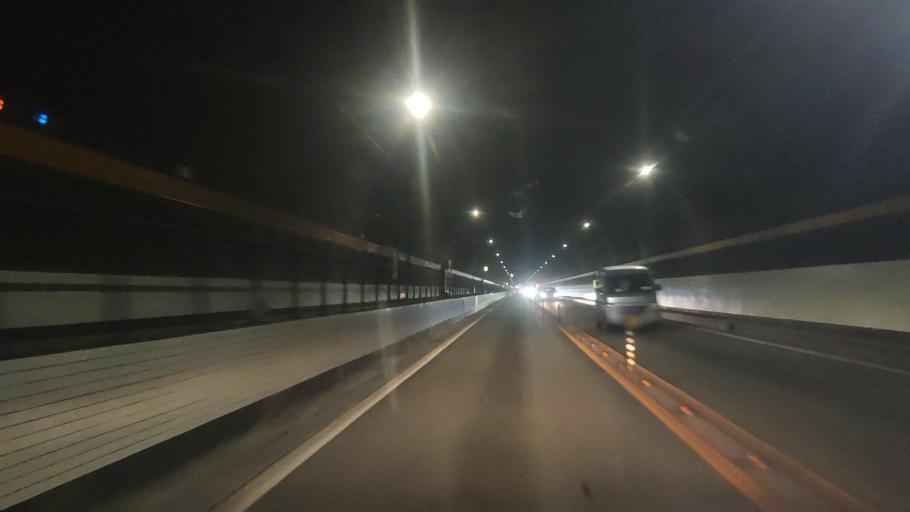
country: JP
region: Nagasaki
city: Nagasaki-shi
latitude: 32.7774
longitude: 129.8875
